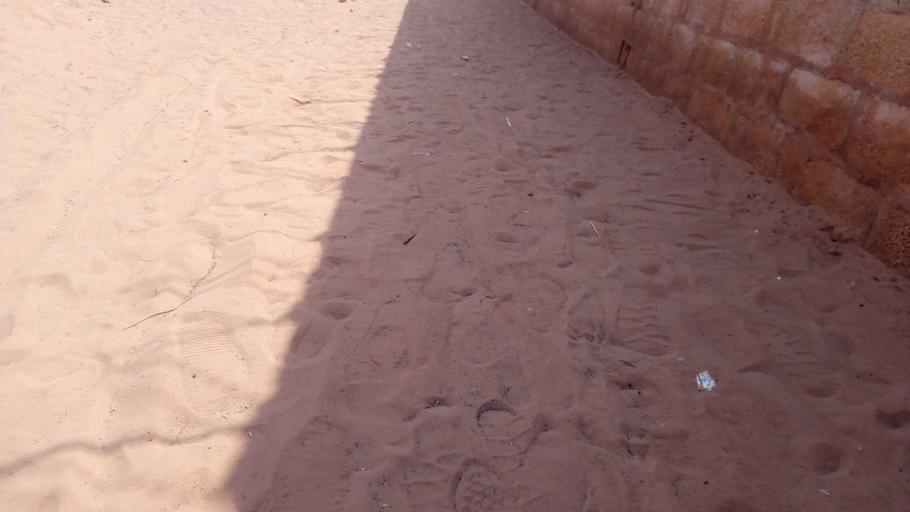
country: ZM
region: Lusaka
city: Lusaka
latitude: -15.3562
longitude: 28.2985
